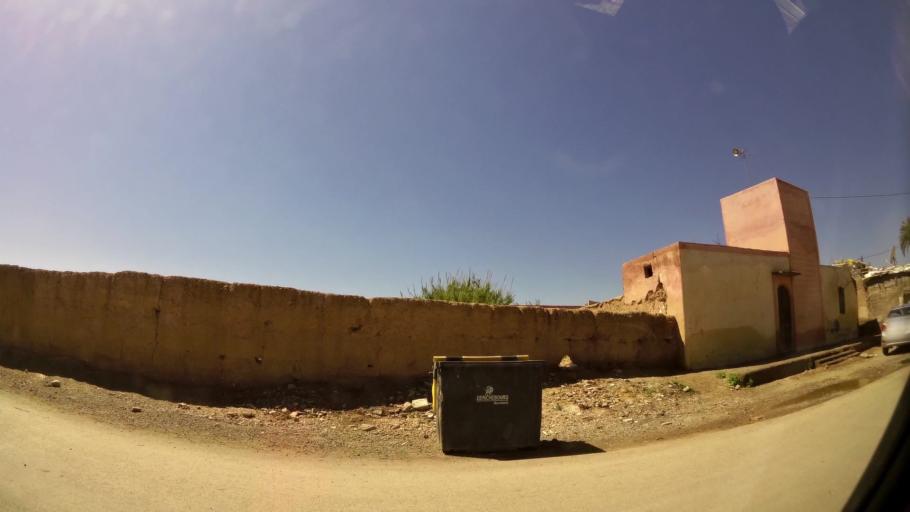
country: MA
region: Marrakech-Tensift-Al Haouz
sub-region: Marrakech
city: Marrakesh
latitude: 31.6700
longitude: -7.9766
